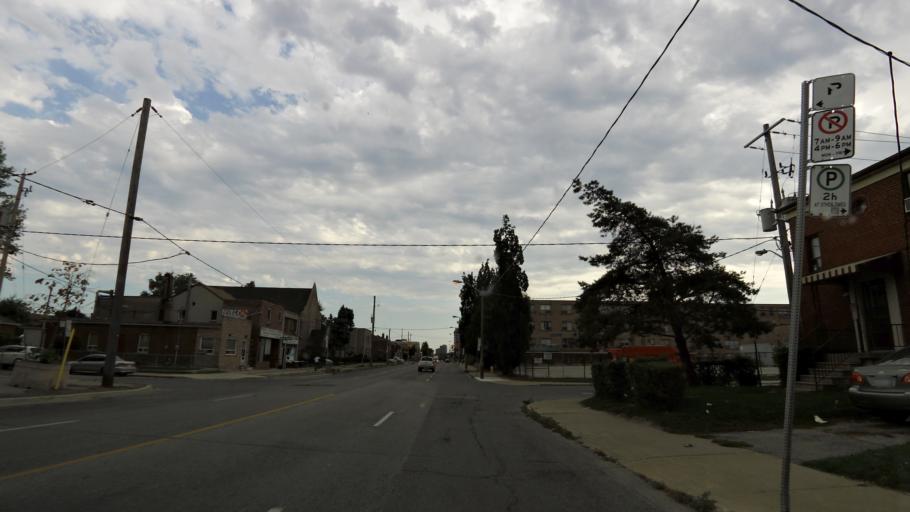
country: CA
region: Ontario
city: Toronto
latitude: 43.6860
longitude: -79.4734
